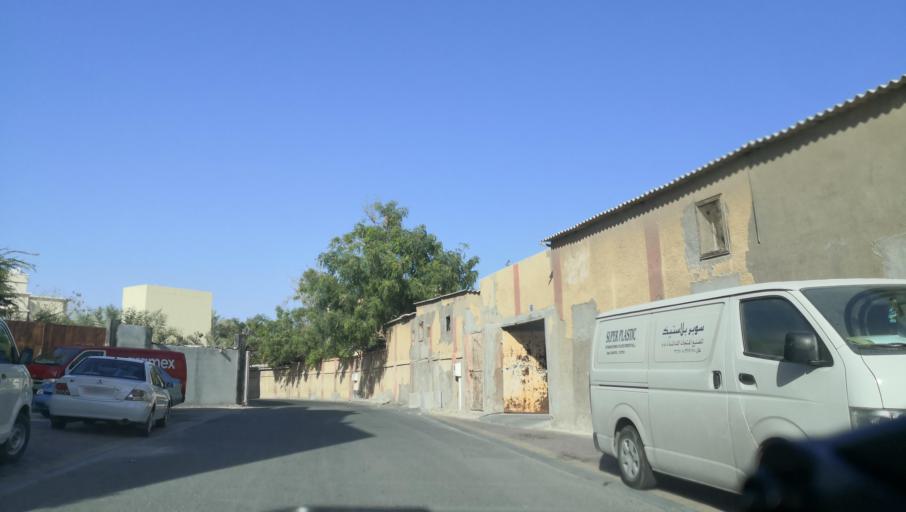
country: BH
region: Muharraq
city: Al Muharraq
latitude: 26.2536
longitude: 50.6336
